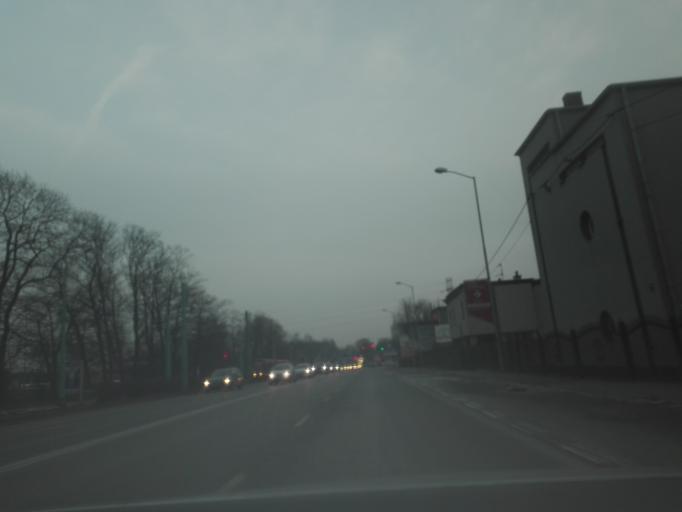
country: PL
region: Silesian Voivodeship
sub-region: Chorzow
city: Chorzow
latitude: 50.2893
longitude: 18.9649
